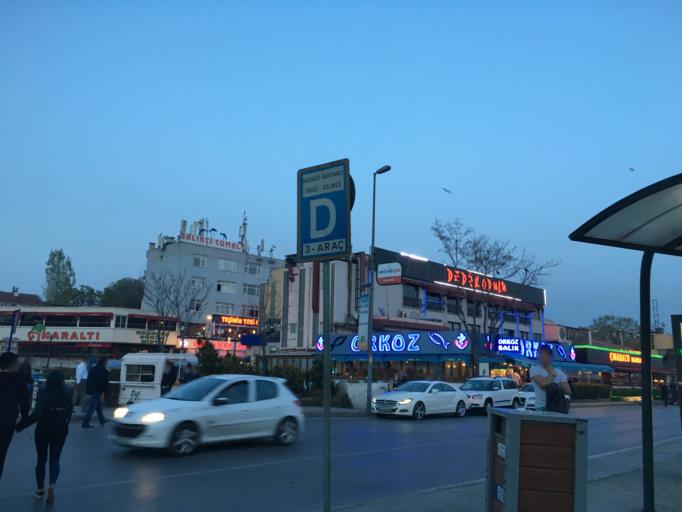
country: TR
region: Istanbul
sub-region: Atasehir
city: Atasehir
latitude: 40.9530
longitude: 29.0956
